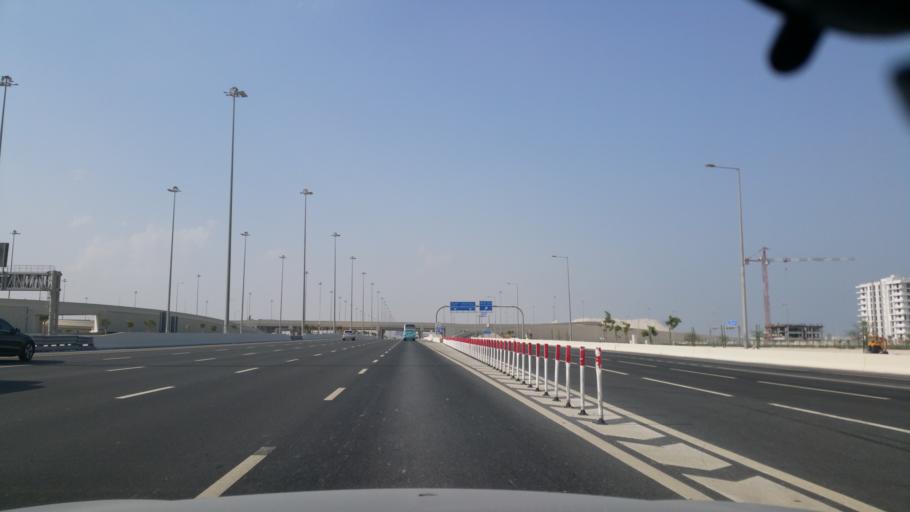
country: QA
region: Baladiyat Umm Salal
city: Umm Salal Muhammad
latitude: 25.4253
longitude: 51.4857
